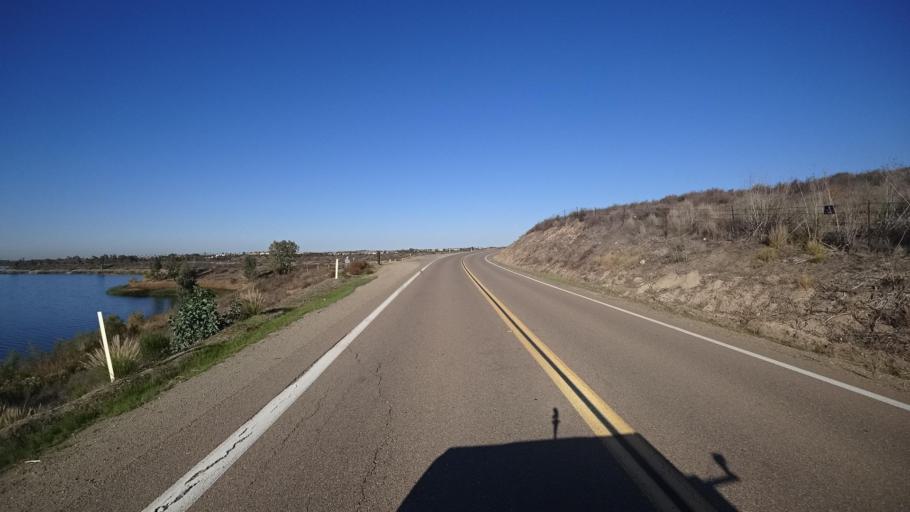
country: US
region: California
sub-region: San Diego County
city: Jamul
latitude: 32.6344
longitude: -116.9197
